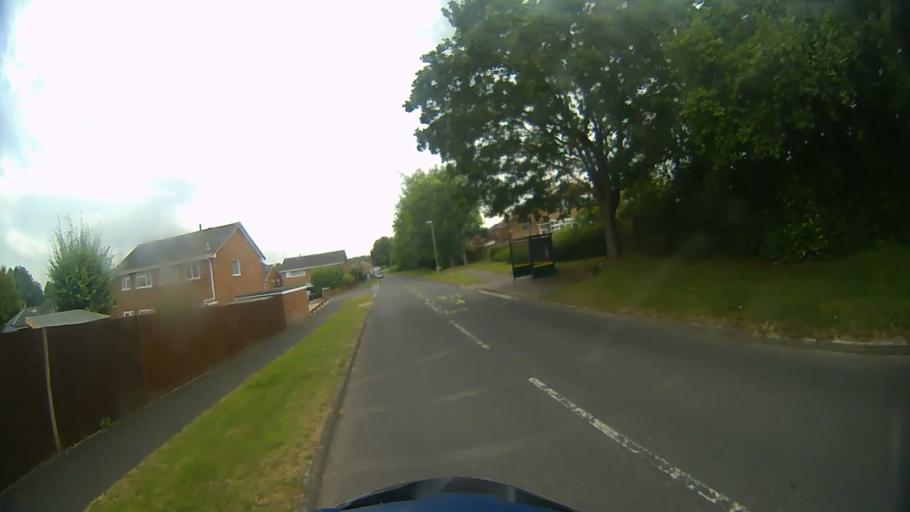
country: GB
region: England
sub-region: Hampshire
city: Basingstoke
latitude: 51.2469
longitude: -1.1101
